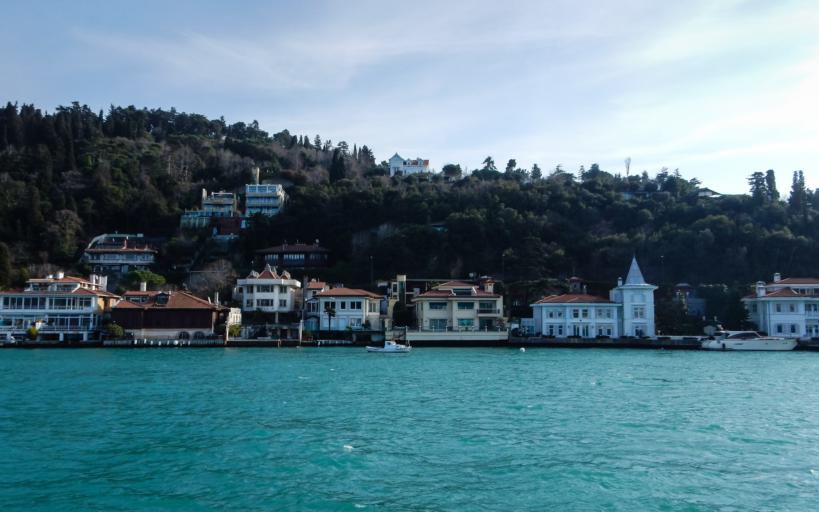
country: TR
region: Istanbul
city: UEskuedar
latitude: 41.0636
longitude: 29.0528
